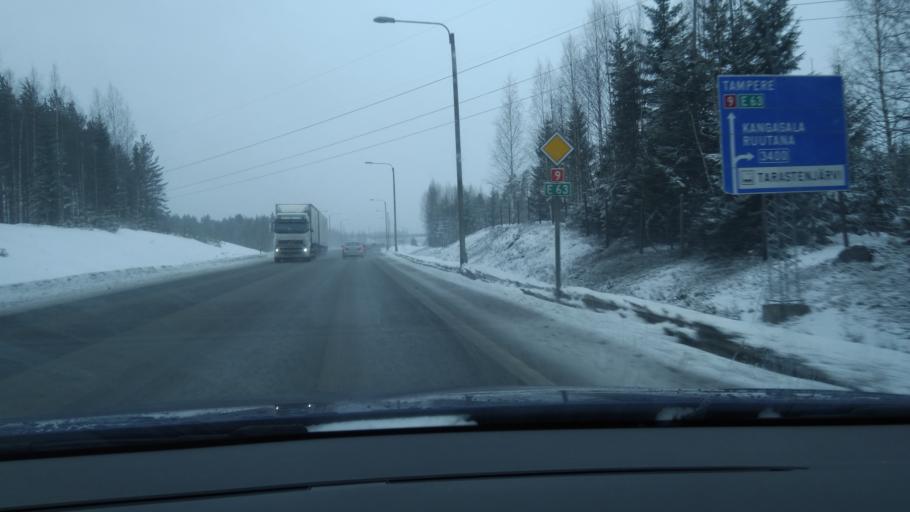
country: FI
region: Pirkanmaa
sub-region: Tampere
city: Kangasala
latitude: 61.5371
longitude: 23.9903
